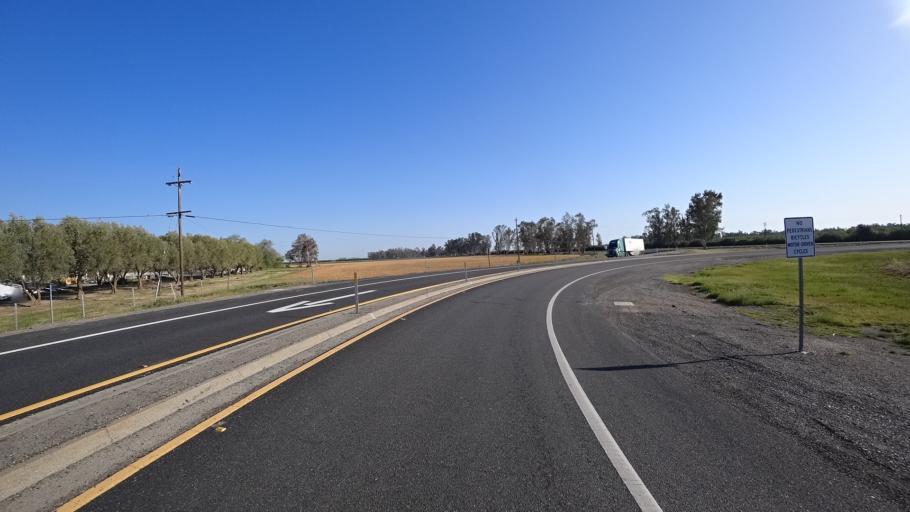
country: US
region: California
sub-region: Glenn County
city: Willows
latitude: 39.5829
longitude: -122.2120
